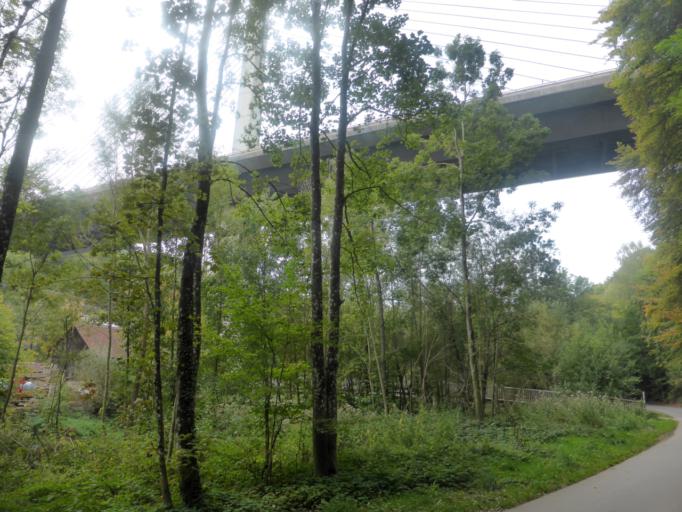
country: LU
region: Luxembourg
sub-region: Canton de Luxembourg
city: Hesperange
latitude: 49.5797
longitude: 6.1520
